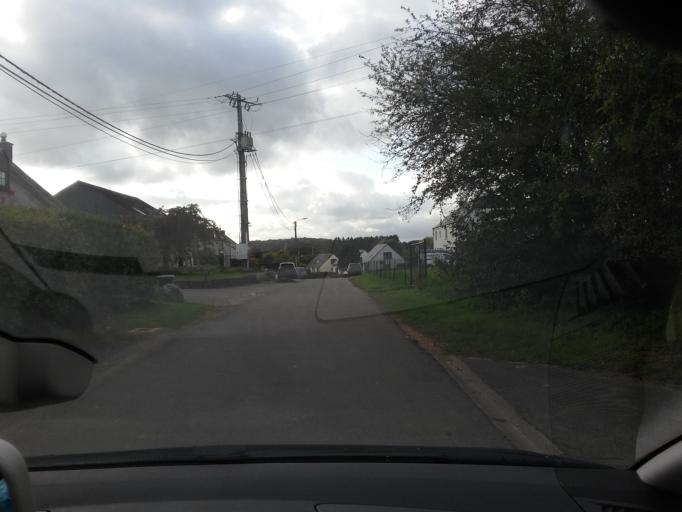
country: BE
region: Wallonia
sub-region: Province du Luxembourg
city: Arlon
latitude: 49.7101
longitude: 5.8269
